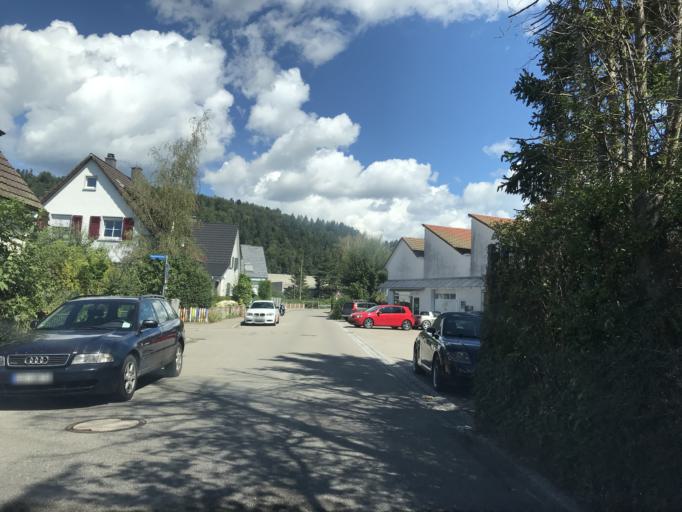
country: DE
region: Baden-Wuerttemberg
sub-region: Freiburg Region
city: Schopfheim
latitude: 47.6451
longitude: 7.8115
